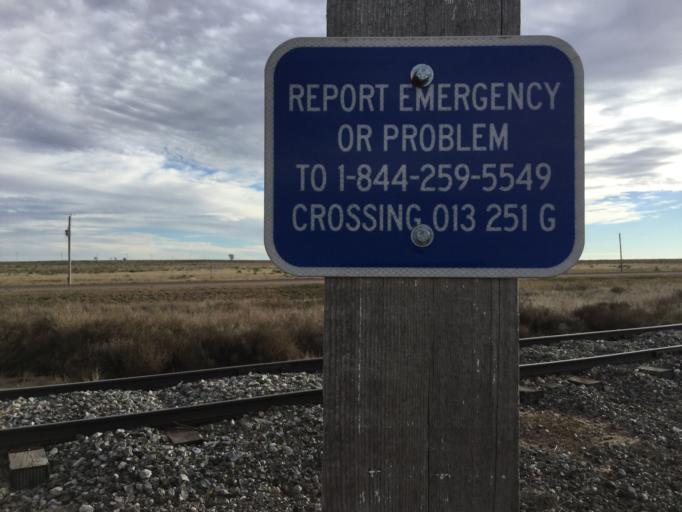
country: US
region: Kansas
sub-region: Morton County
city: Elkhart
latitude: 37.0250
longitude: -101.8675
